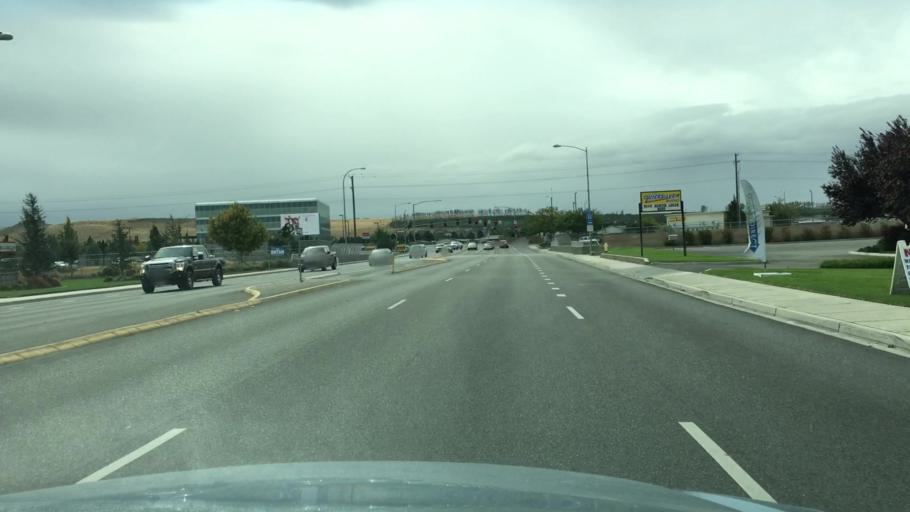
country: US
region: Washington
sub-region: Franklin County
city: West Pasco
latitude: 46.2118
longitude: -119.2257
